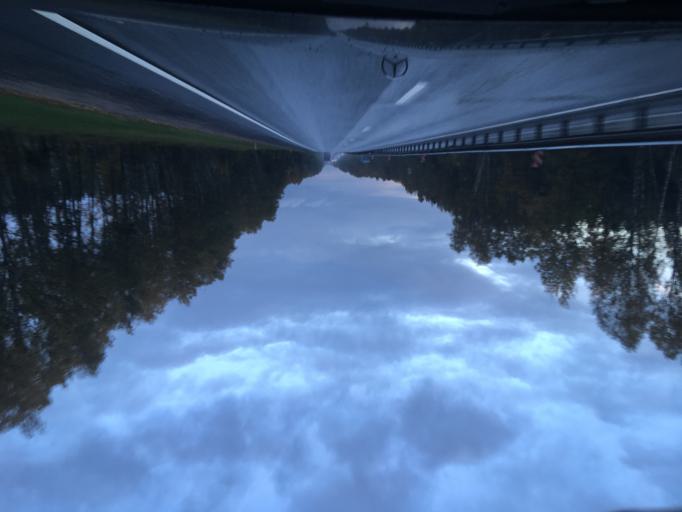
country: RU
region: Smolensk
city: Yartsevo
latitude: 55.0864
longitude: 32.7967
